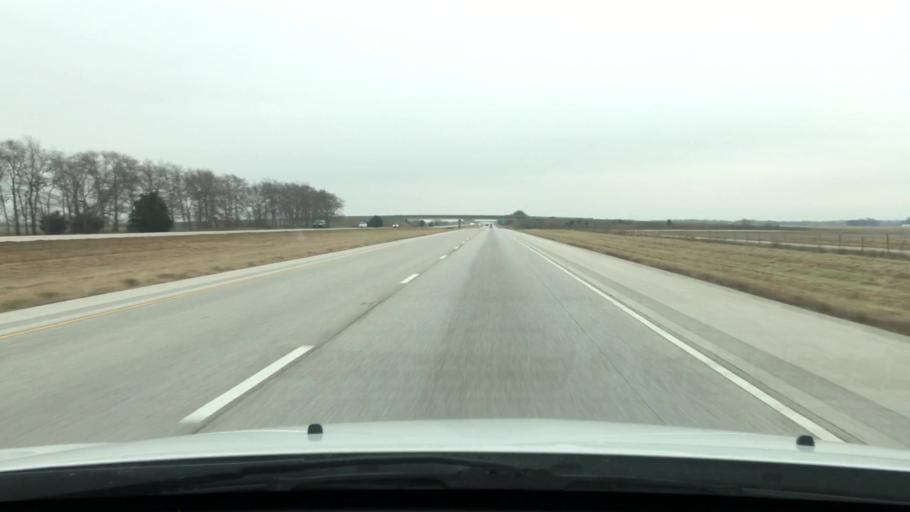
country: US
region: Illinois
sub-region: Scott County
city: Winchester
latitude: 39.6801
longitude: -90.3532
